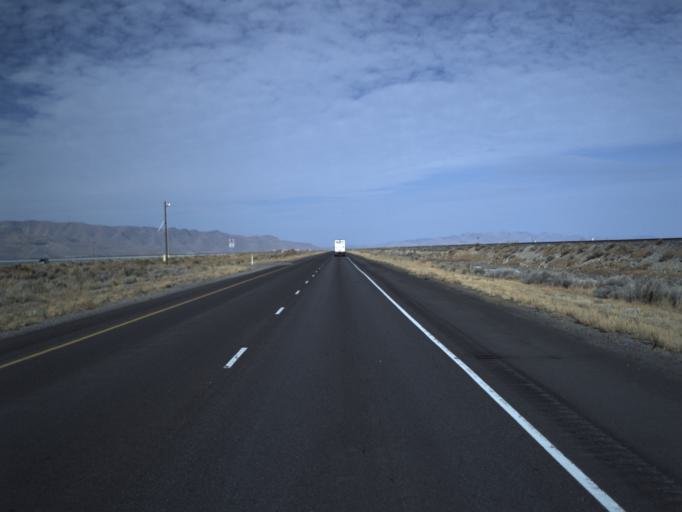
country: US
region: Utah
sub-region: Tooele County
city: Stansbury park
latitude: 40.6688
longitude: -112.3778
